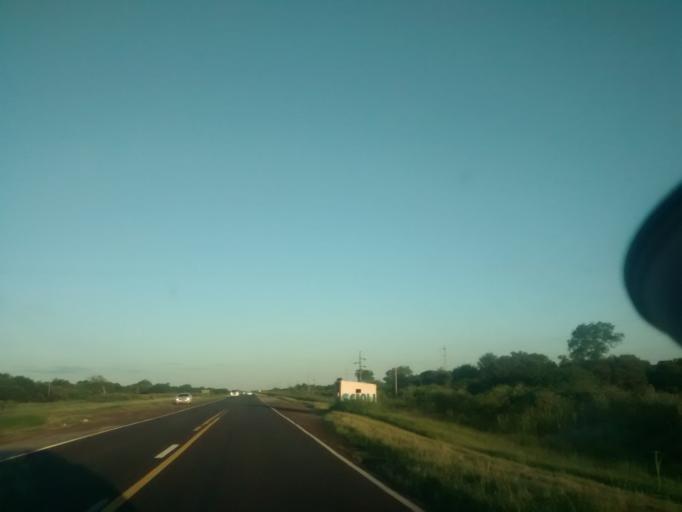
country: AR
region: Chaco
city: La Escondida
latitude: -27.0862
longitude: -59.6459
